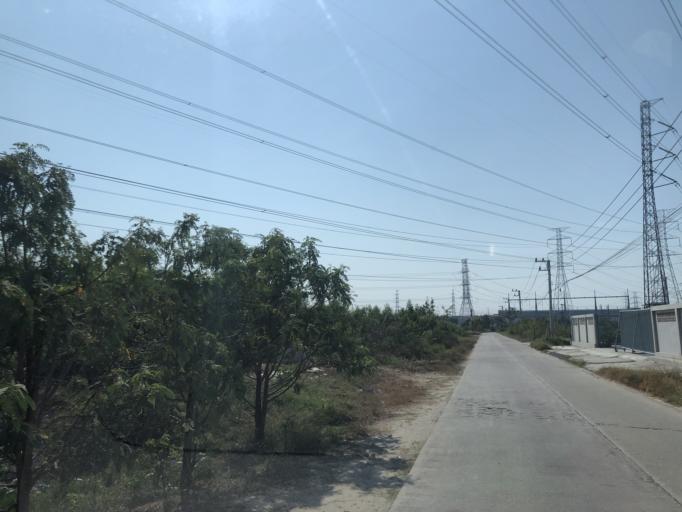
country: TH
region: Chachoengsao
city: Bang Pakong
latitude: 13.5146
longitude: 101.0239
